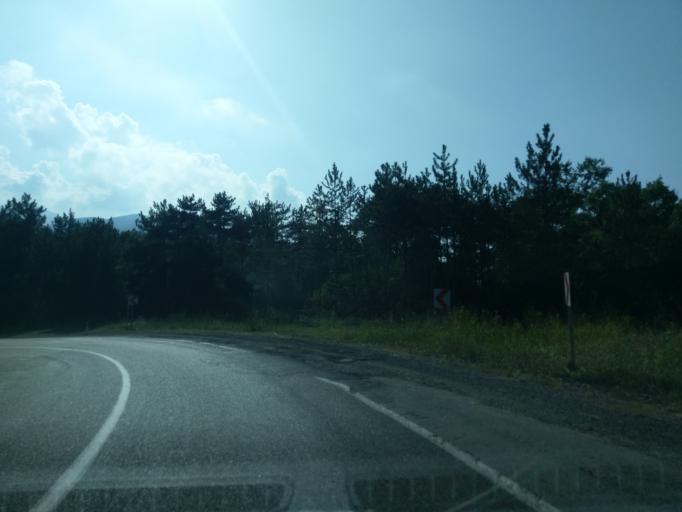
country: TR
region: Sinop
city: Yenikonak
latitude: 41.9426
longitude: 34.7078
